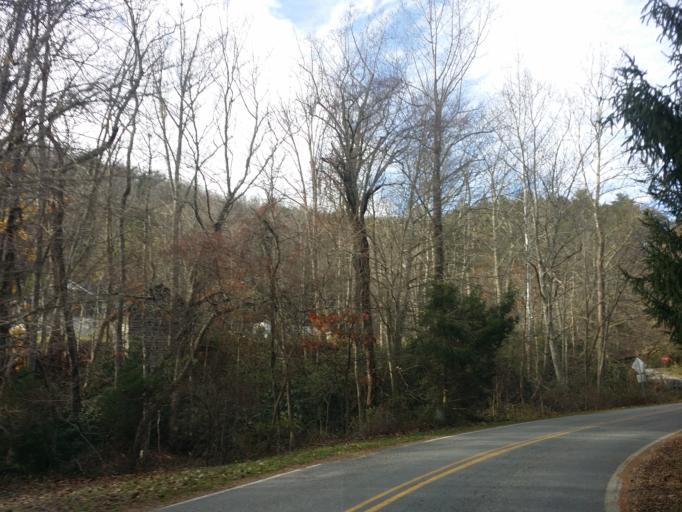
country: US
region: North Carolina
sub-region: Buncombe County
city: Swannanoa
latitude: 35.6332
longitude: -82.4171
